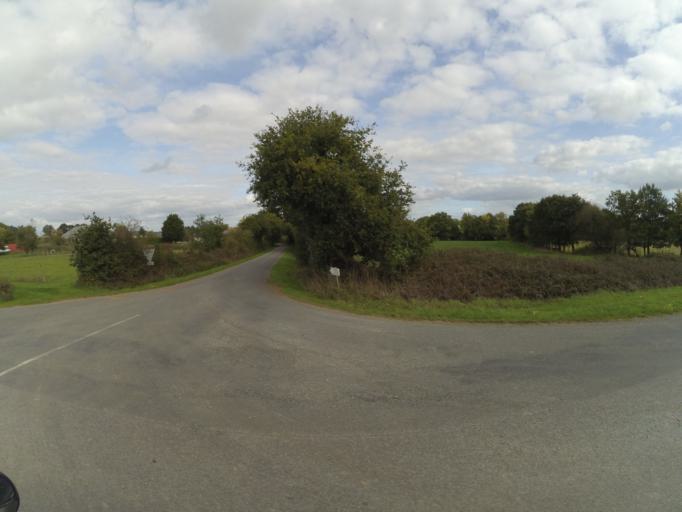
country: FR
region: Pays de la Loire
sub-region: Departement de la Loire-Atlantique
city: Bouvron
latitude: 47.4679
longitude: -1.8362
